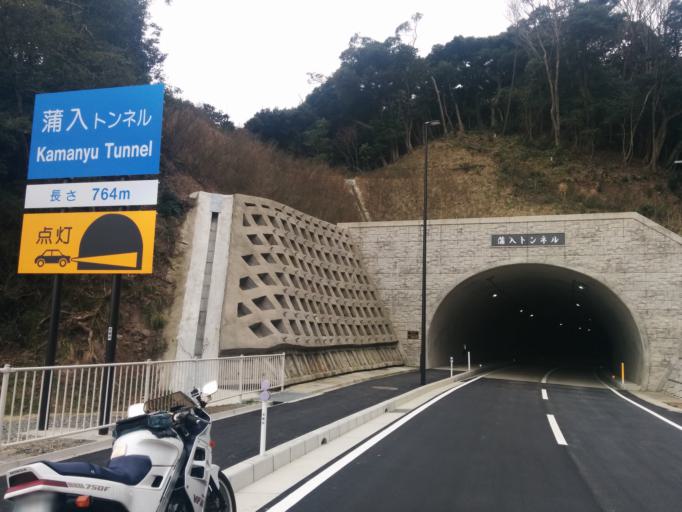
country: JP
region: Kyoto
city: Miyazu
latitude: 35.7446
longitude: 135.2559
